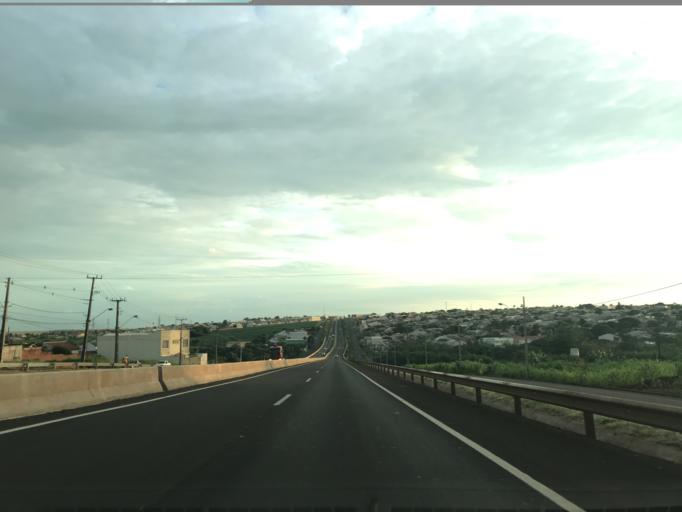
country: BR
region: Parana
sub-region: Maringa
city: Maringa
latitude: -23.3906
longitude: -51.9696
